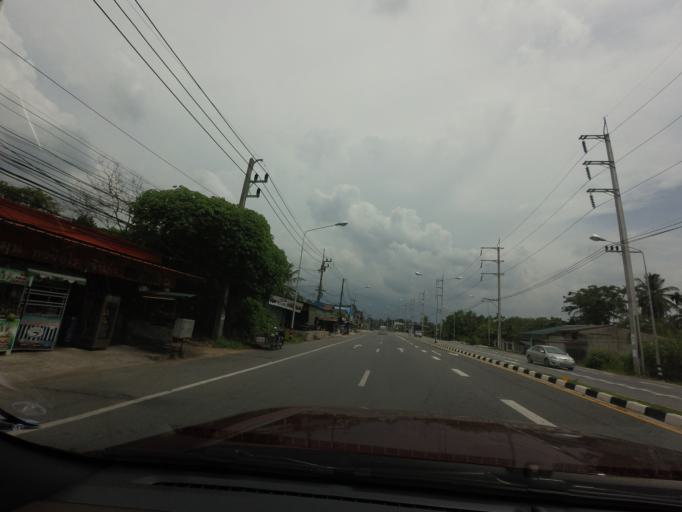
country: TH
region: Yala
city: Yala
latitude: 6.4979
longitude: 101.2666
